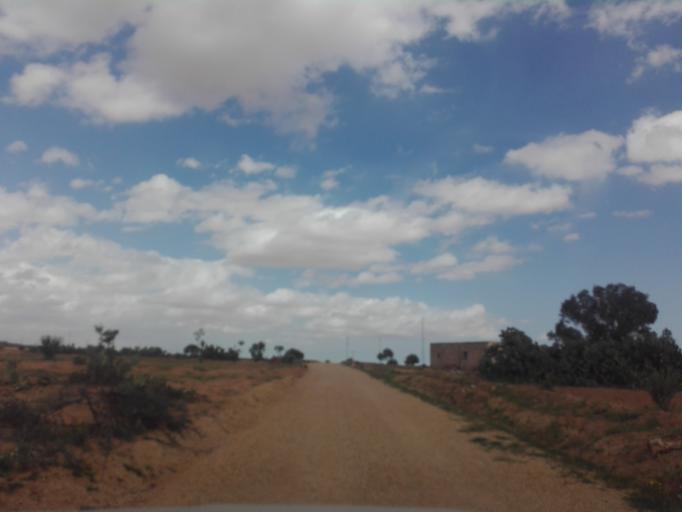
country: TN
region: Safaqis
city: Sfax
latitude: 34.6983
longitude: 10.4321
